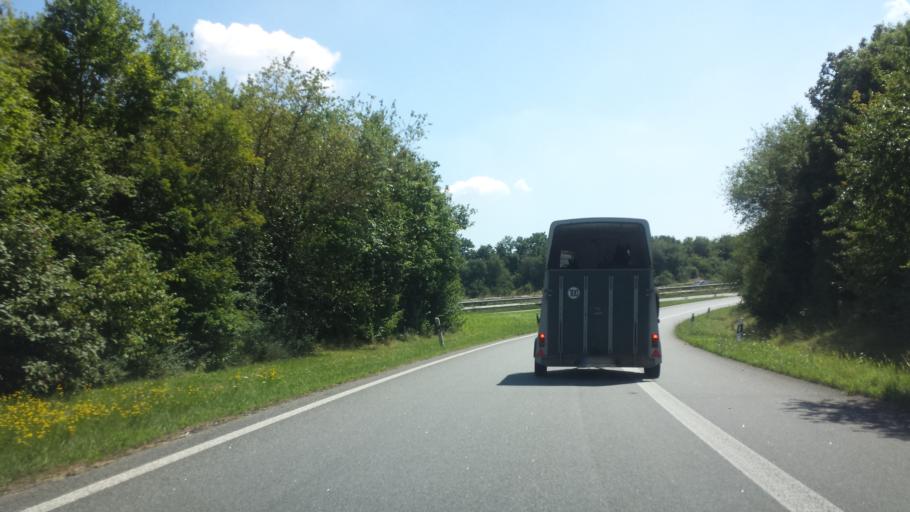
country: DE
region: Rheinland-Pfalz
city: Kleinniedesheim
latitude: 49.6232
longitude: 8.2926
